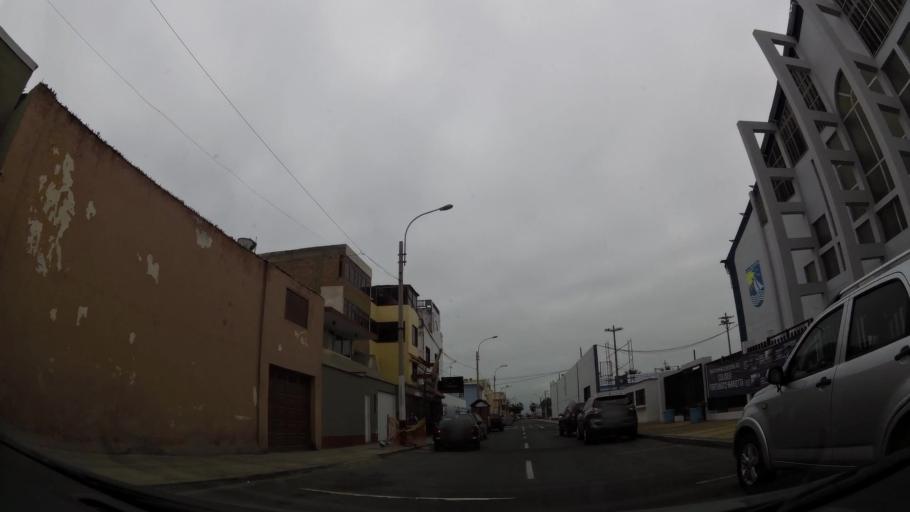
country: PE
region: Callao
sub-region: Callao
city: Callao
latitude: -12.0731
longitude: -77.1618
